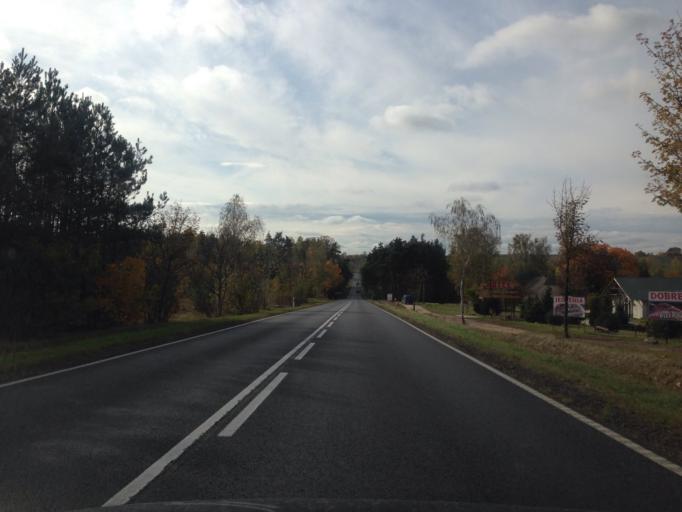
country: PL
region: Kujawsko-Pomorskie
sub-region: Powiat brodnicki
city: Brzozie
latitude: 53.3166
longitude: 19.5269
